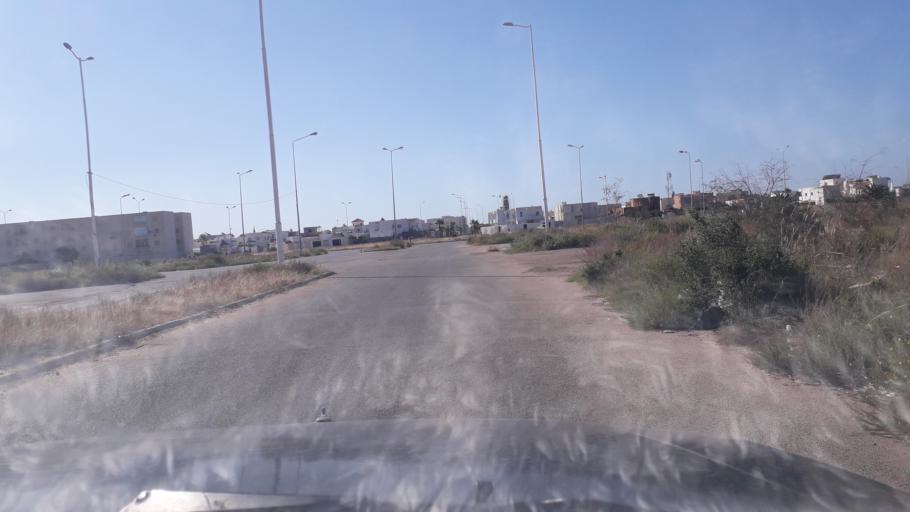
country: TN
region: Safaqis
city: Al Qarmadah
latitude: 34.8327
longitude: 10.7550
